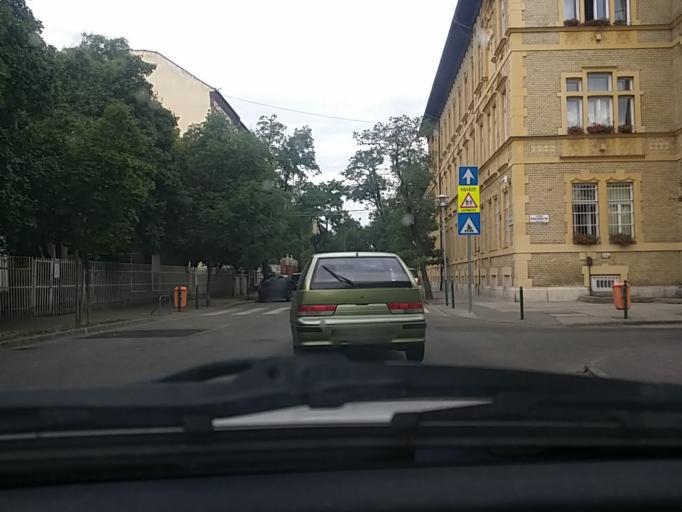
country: HU
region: Budapest
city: Budapest X. keruelet
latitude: 47.4866
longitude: 19.1313
